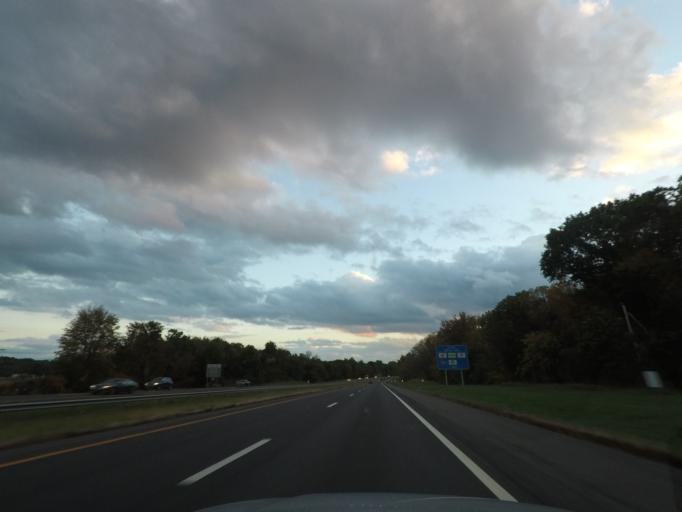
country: US
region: New York
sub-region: Ulster County
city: Glasco
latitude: 42.0344
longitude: -73.9912
